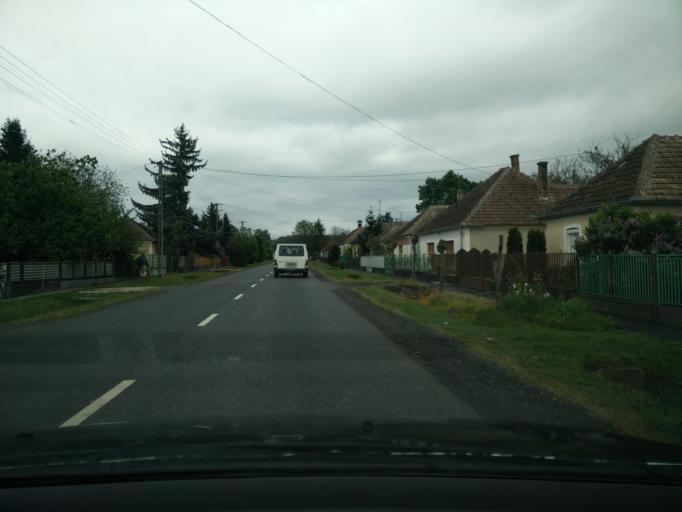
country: HU
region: Zala
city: Turje
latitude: 46.9821
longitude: 17.1114
